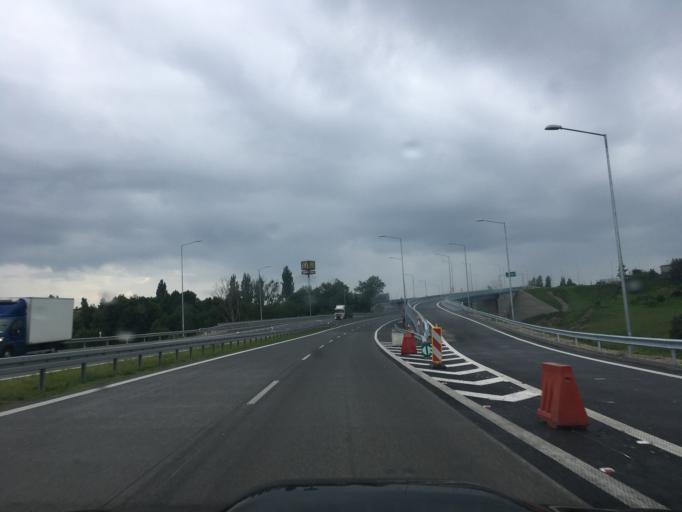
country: PL
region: Masovian Voivodeship
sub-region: Powiat piaseczynski
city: Gora Kalwaria
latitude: 51.9707
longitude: 21.2188
